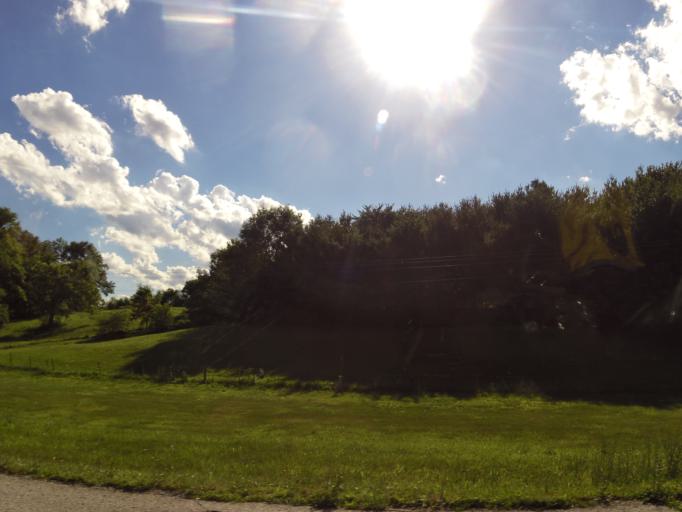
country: US
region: Missouri
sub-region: Marion County
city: Palmyra
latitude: 39.8466
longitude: -91.5250
